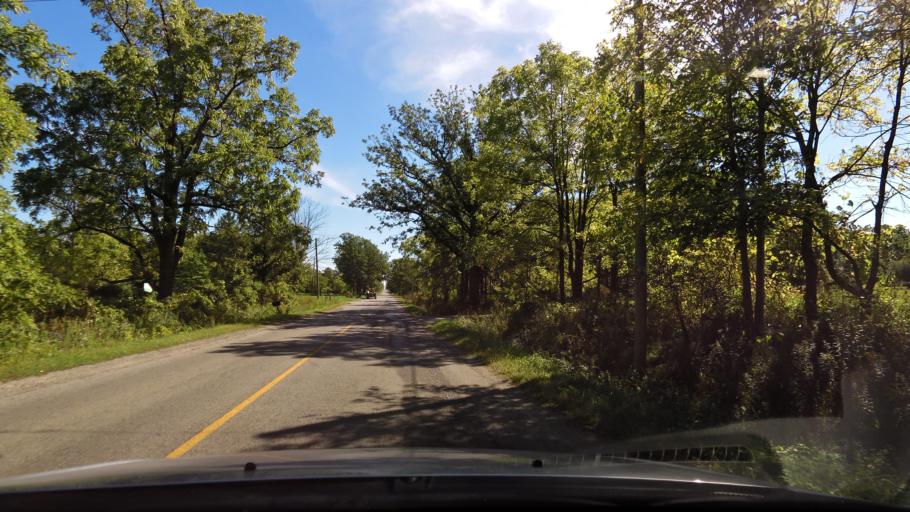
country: CA
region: Ontario
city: Ancaster
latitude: 43.0794
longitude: -80.0908
